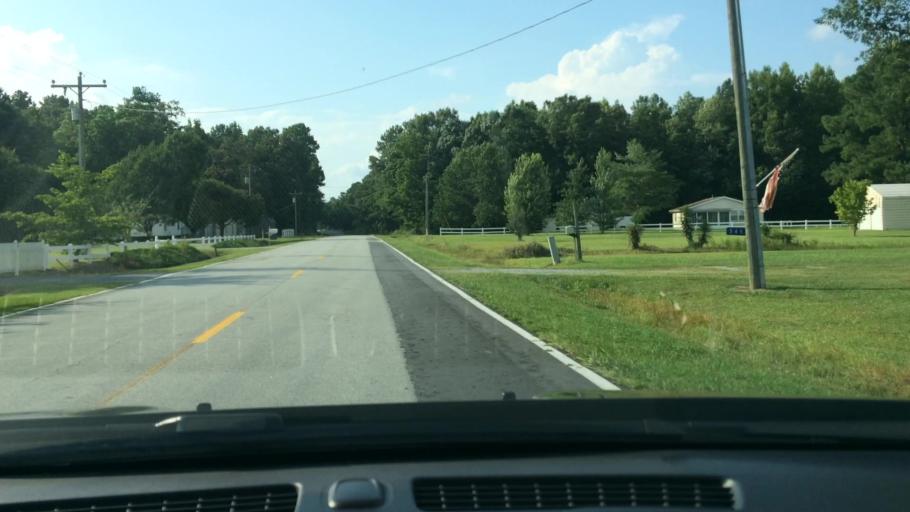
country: US
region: North Carolina
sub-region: Beaufort County
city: River Road
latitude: 35.4479
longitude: -77.0153
